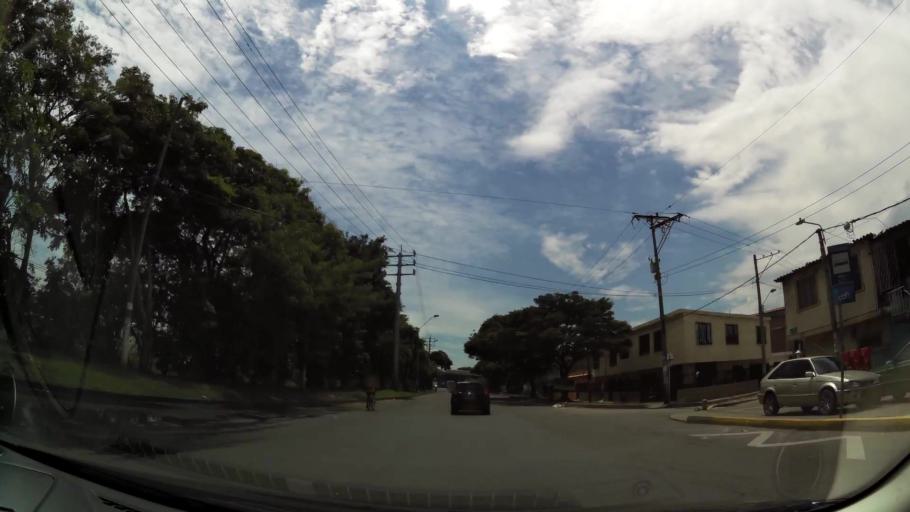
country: CO
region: Valle del Cauca
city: Cali
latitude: 3.4458
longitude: -76.4842
